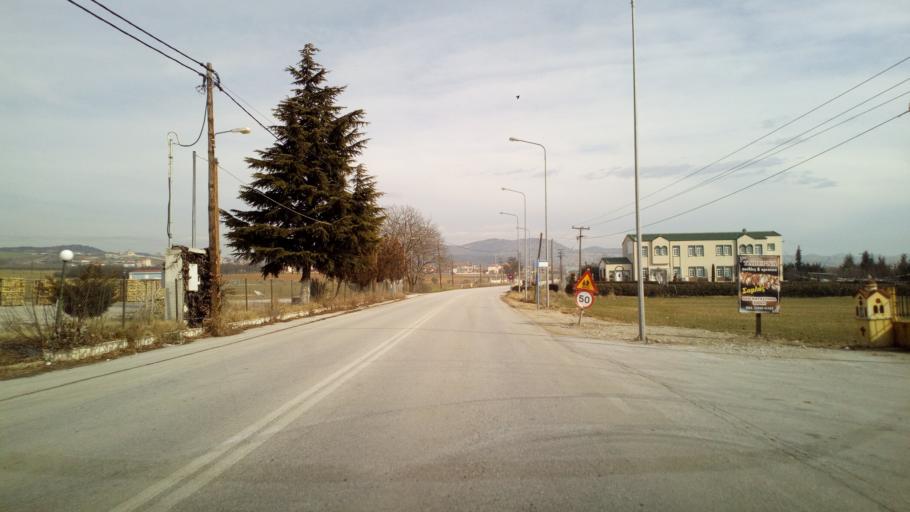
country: GR
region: Central Macedonia
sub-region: Nomos Thessalonikis
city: Kolchikon
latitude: 40.7548
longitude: 23.1188
